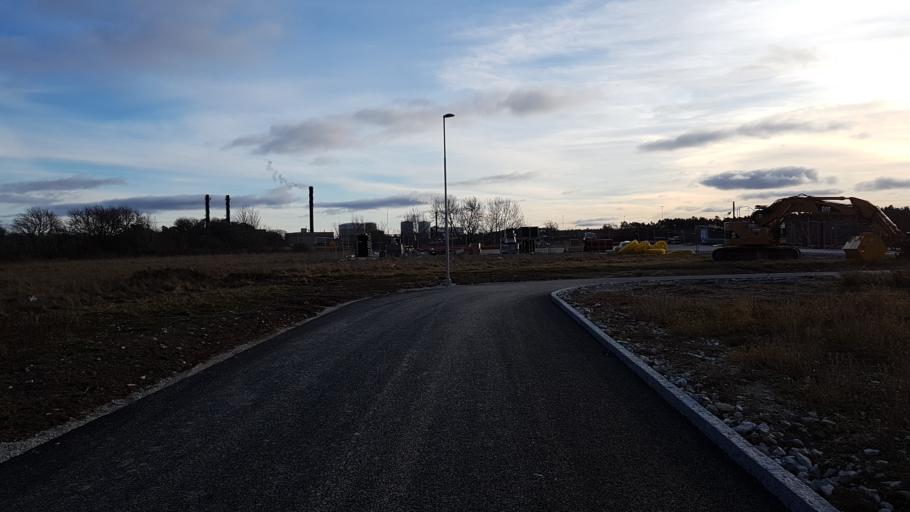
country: SE
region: Gotland
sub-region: Gotland
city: Visby
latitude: 57.6269
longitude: 18.3121
